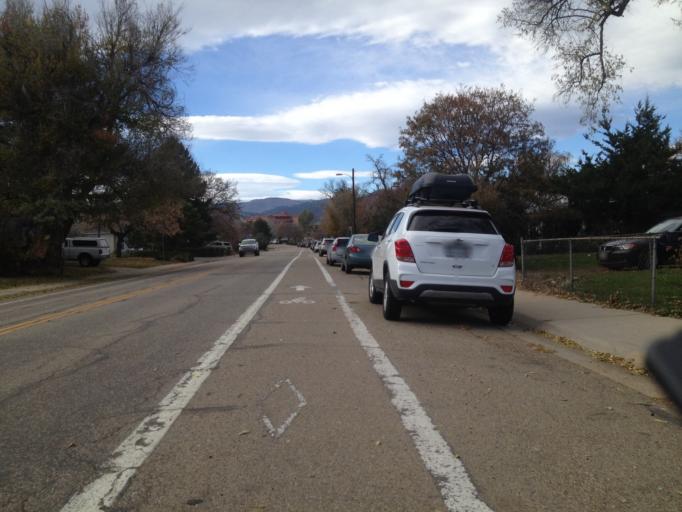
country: US
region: Colorado
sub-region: Boulder County
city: Boulder
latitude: 39.9977
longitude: -105.2558
